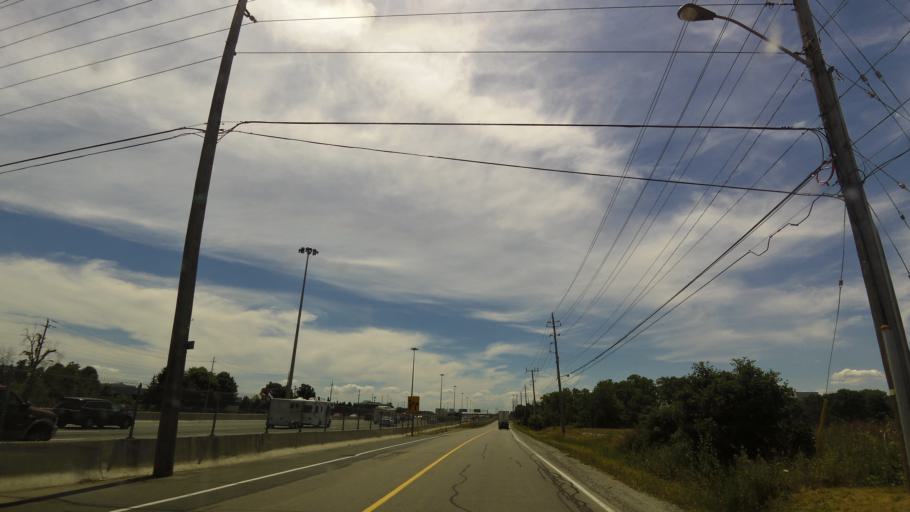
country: CA
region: Ontario
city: Burlington
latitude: 43.3870
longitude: -79.7660
